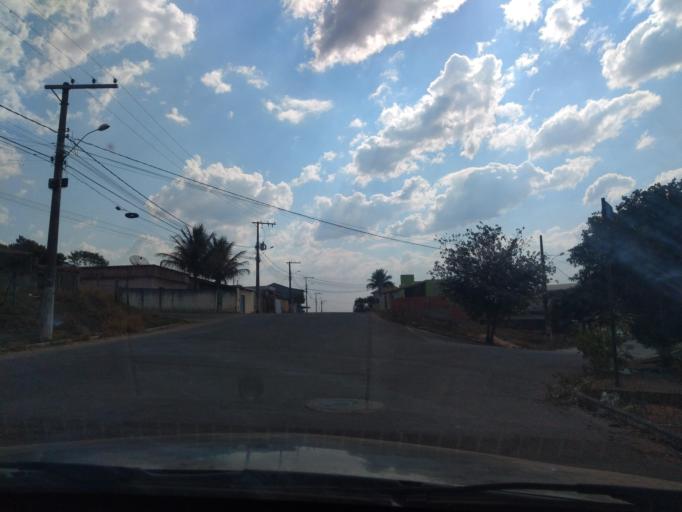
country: BR
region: Minas Gerais
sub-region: Tres Coracoes
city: Tres Coracoes
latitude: -21.6835
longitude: -45.2355
